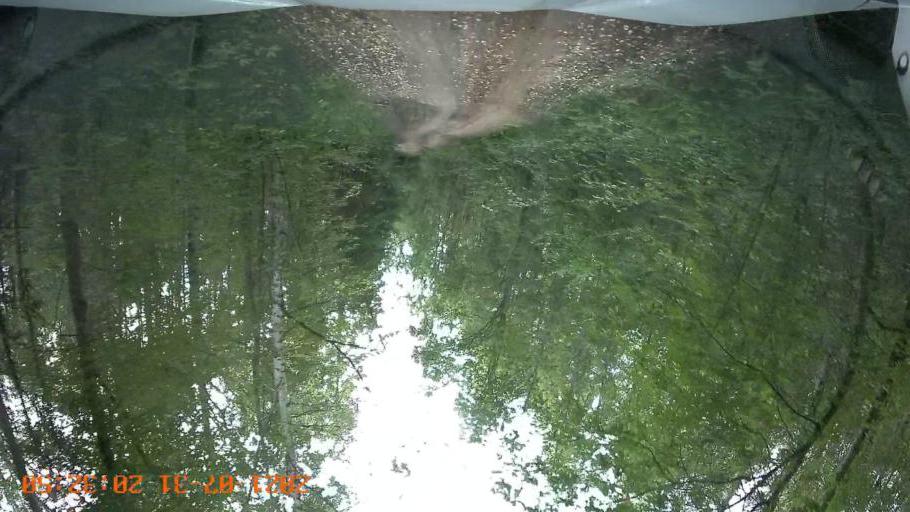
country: RU
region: Republic of Karelia
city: Shal'skiy
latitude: 61.6616
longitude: 36.2717
